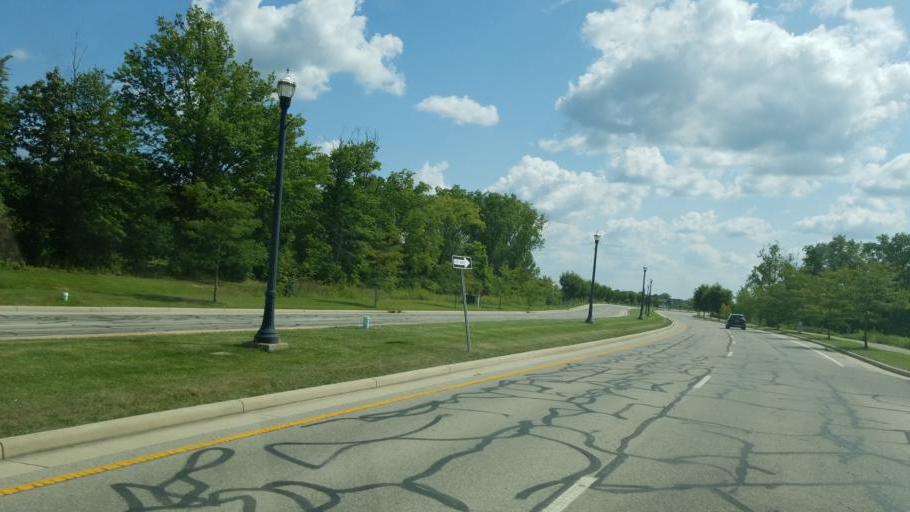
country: US
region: Ohio
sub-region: Delaware County
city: Lewis Center
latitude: 40.2382
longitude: -83.0355
